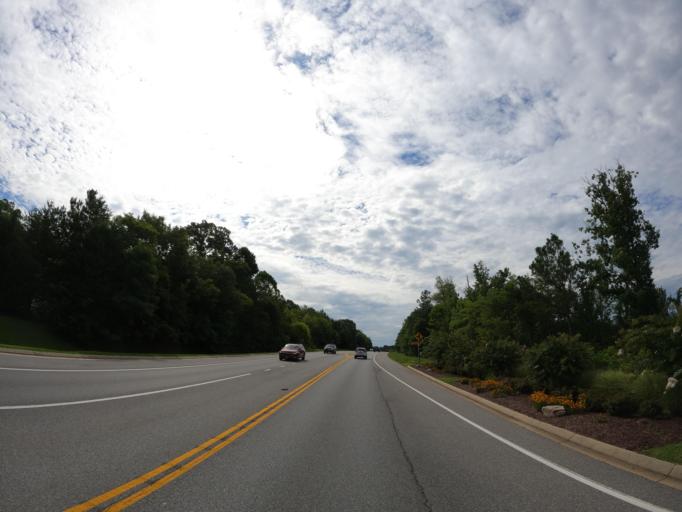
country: US
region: Maryland
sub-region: Saint Mary's County
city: Leonardtown
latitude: 38.2929
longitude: -76.6276
